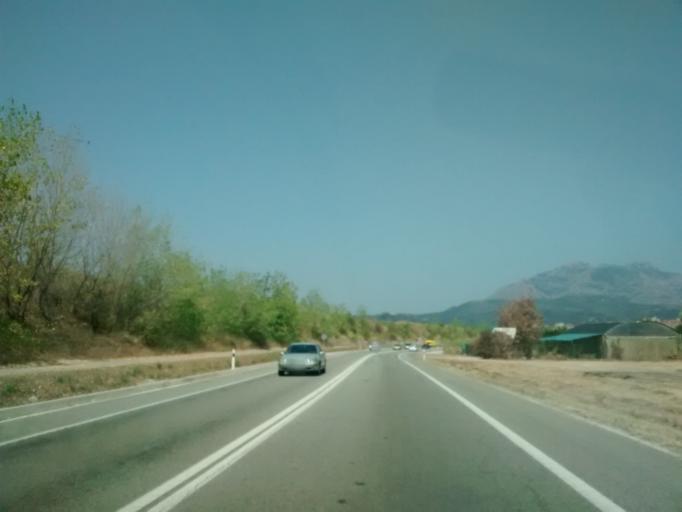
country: ES
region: Catalonia
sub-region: Provincia de Barcelona
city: Olesa de Montserrat
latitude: 41.5319
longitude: 1.9030
